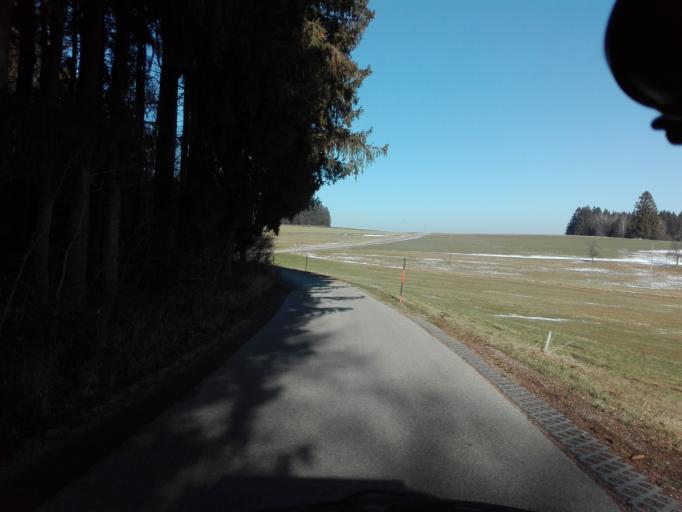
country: AT
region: Upper Austria
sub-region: Politischer Bezirk Urfahr-Umgebung
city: Sonnberg im Muehlkreis
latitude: 48.4635
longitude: 14.3278
